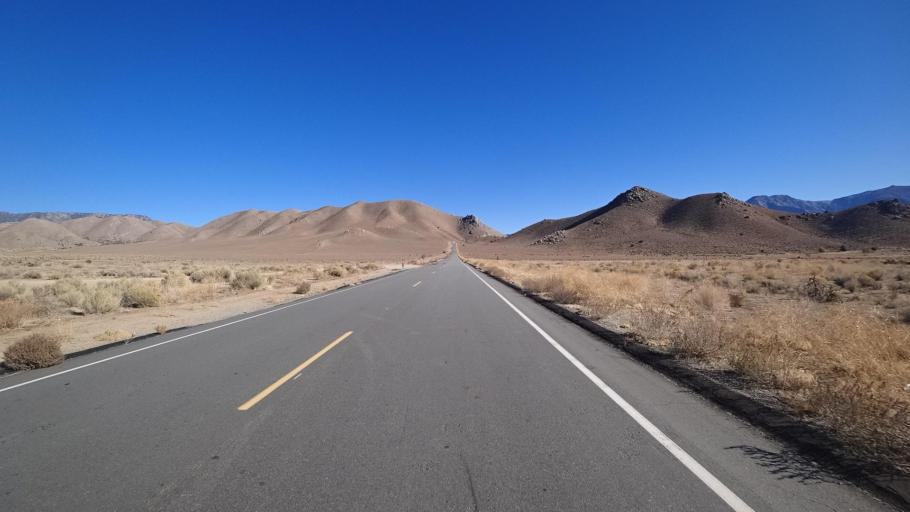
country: US
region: California
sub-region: Kern County
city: Weldon
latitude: 35.6805
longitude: -118.3718
